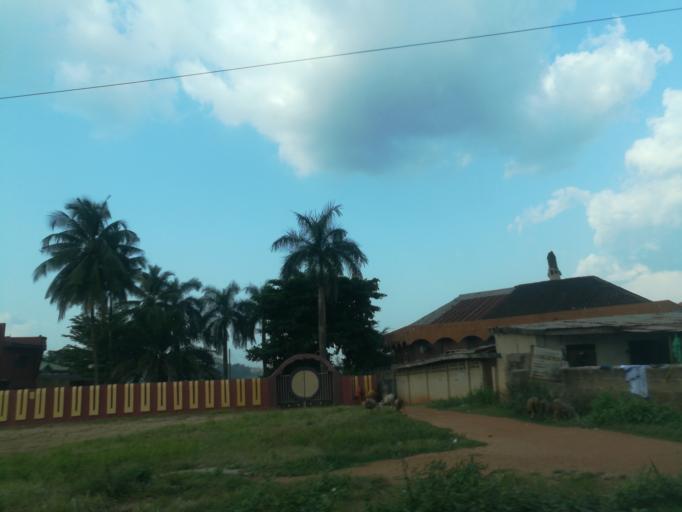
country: NG
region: Oyo
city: Moniya
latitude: 7.4788
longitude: 3.9114
